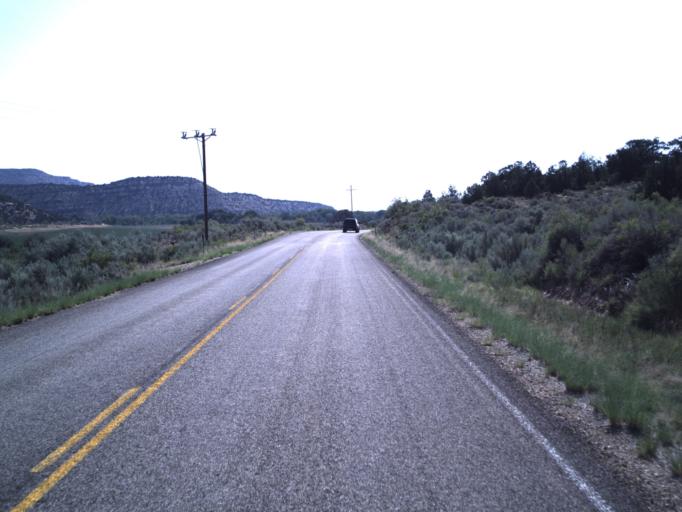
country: US
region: Utah
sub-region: Duchesne County
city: Duchesne
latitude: 40.2952
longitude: -110.5111
